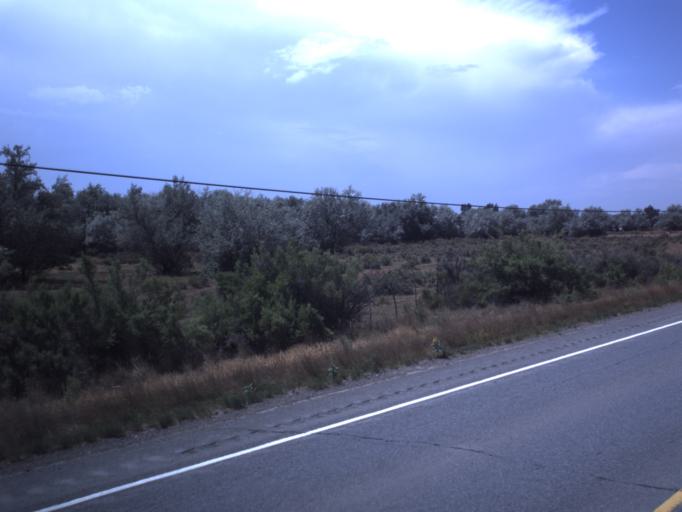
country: US
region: Utah
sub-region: Duchesne County
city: Roosevelt
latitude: 40.3020
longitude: -109.8039
